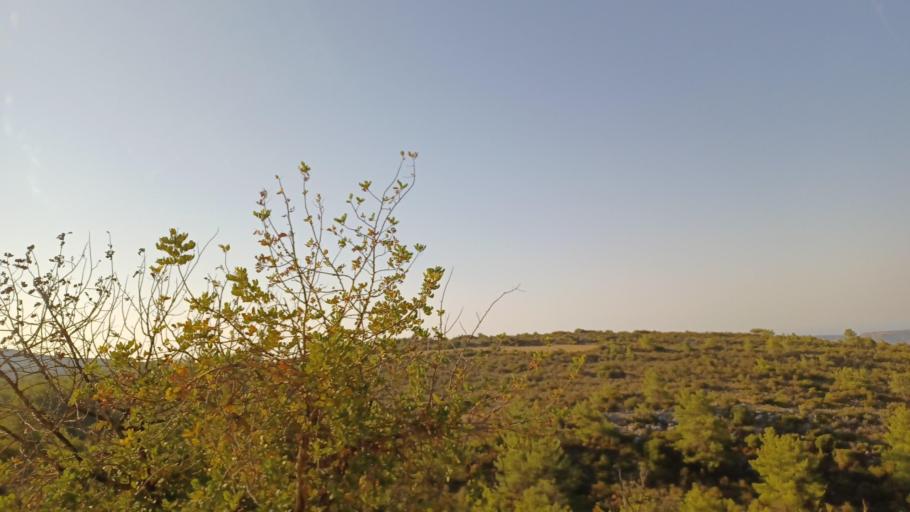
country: CY
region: Limassol
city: Pissouri
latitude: 34.7283
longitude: 32.6750
